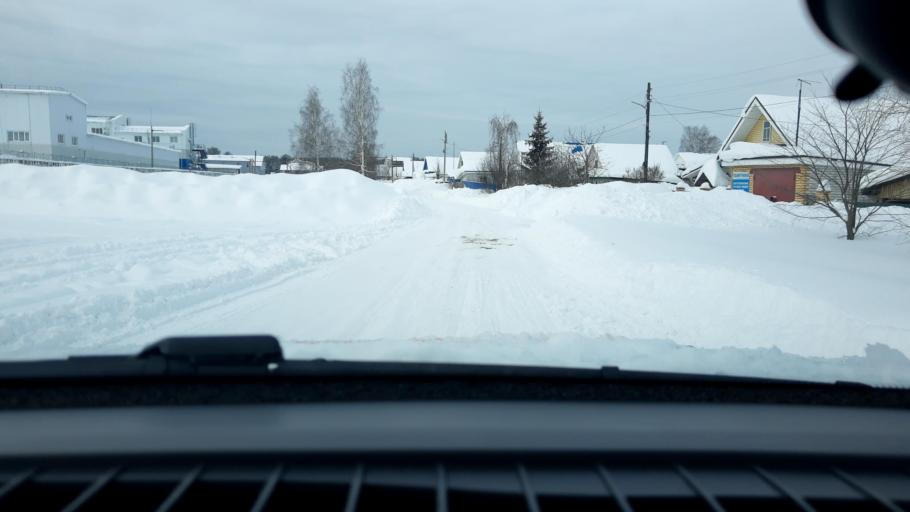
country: RU
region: Nizjnij Novgorod
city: Lukino
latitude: 56.3963
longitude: 43.7004
